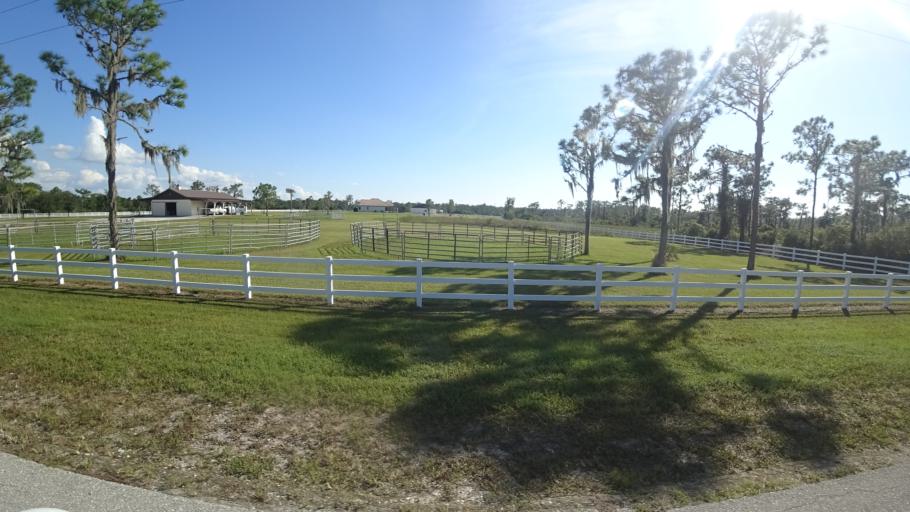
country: US
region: Florida
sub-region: Sarasota County
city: Lake Sarasota
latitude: 27.3977
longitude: -82.2852
